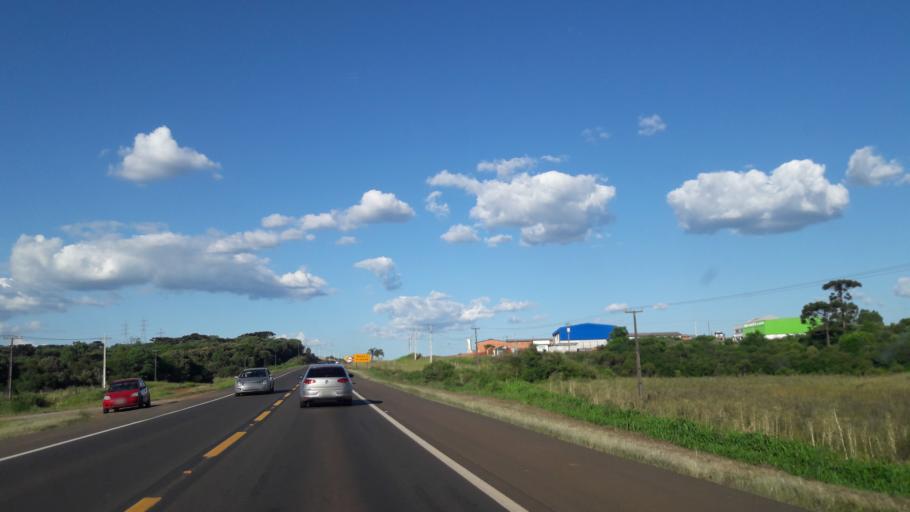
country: BR
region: Parana
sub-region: Guarapuava
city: Guarapuava
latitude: -25.3741
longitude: -51.5016
